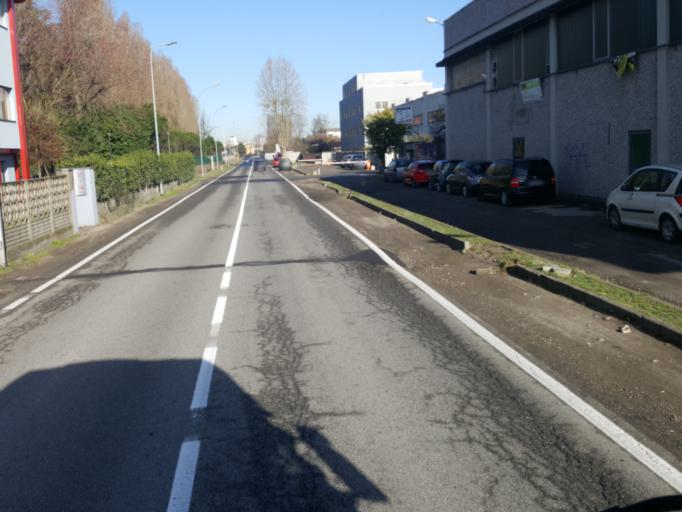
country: IT
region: Lombardy
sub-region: Citta metropolitana di Milano
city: Settala
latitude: 45.4454
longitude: 9.3844
